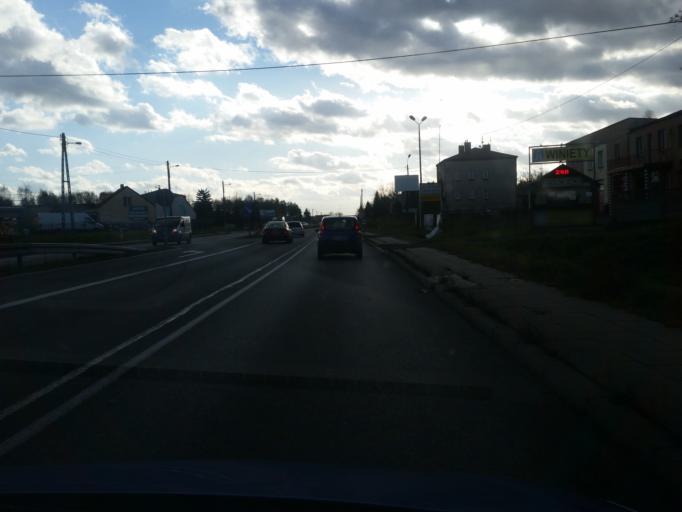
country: PL
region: Silesian Voivodeship
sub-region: Powiat czestochowski
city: Kamienica Polska
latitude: 50.6927
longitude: 19.1362
